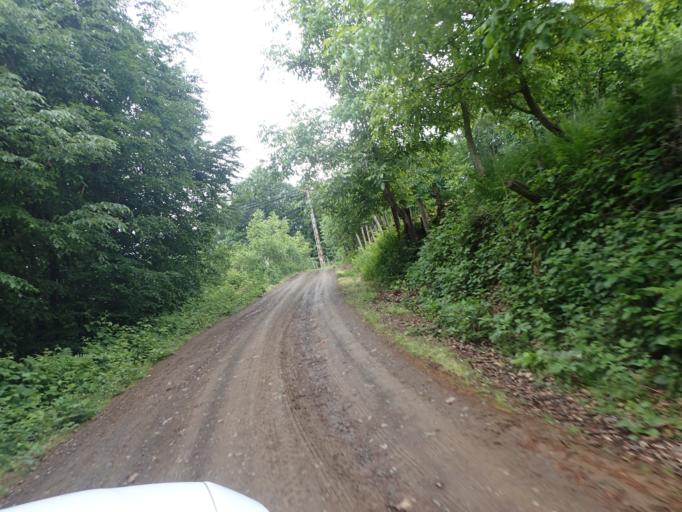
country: TR
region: Samsun
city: Salipazari
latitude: 40.9096
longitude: 36.8743
